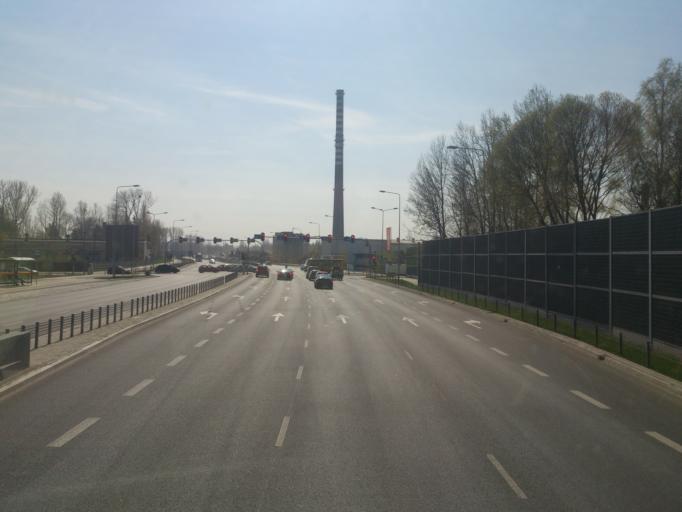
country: PL
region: Lodz Voivodeship
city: Lodz
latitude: 51.7186
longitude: 19.4562
